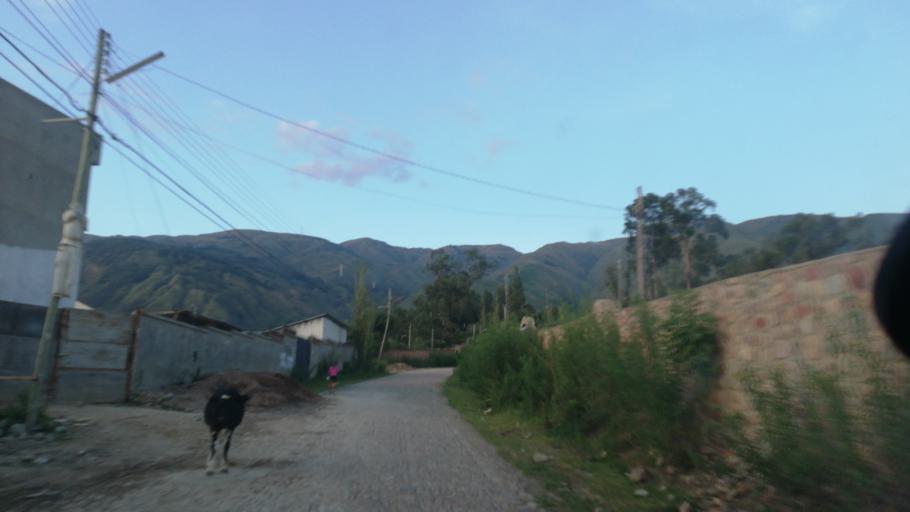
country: BO
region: Cochabamba
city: Cochabamba
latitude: -17.3361
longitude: -66.2099
